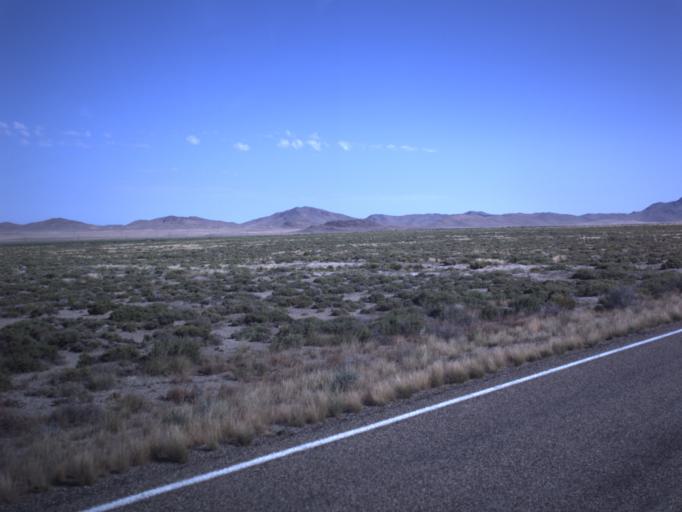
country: US
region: Utah
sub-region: Beaver County
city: Milford
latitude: 38.6403
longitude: -112.9834
